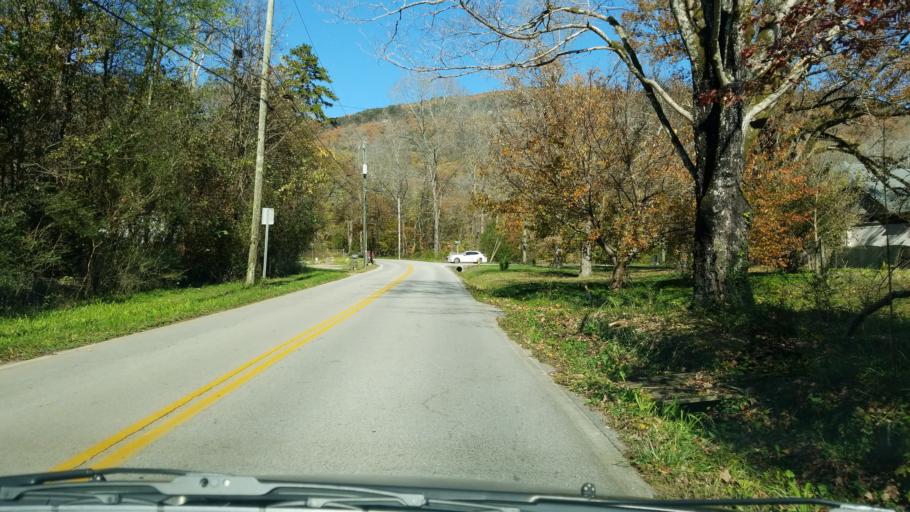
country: US
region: Tennessee
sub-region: Hamilton County
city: Falling Water
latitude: 35.2049
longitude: -85.2546
